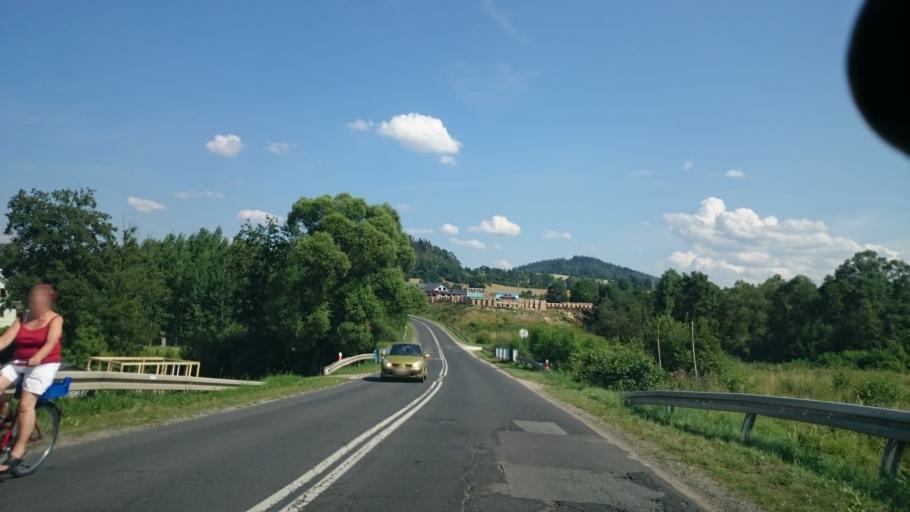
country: PL
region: Lower Silesian Voivodeship
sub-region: Powiat klodzki
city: Ladek-Zdroj
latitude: 50.3399
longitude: 16.8037
